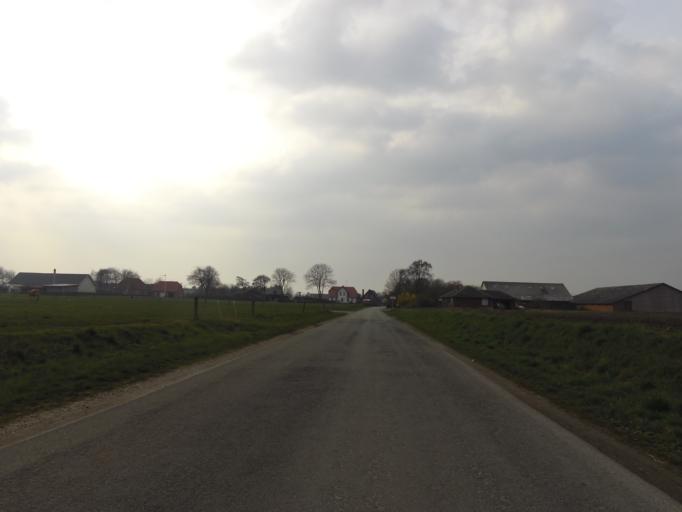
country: DK
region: South Denmark
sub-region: Esbjerg Kommune
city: Ribe
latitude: 55.3537
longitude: 8.7365
